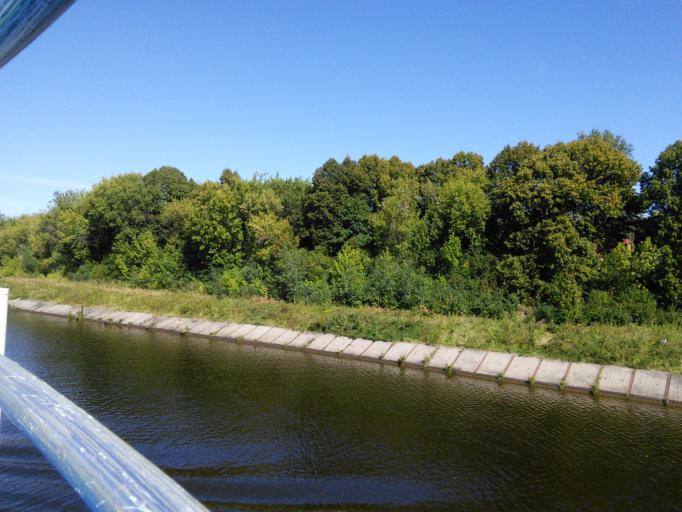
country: RU
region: Moskovskaya
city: Yermolino
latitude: 56.1533
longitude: 37.5125
